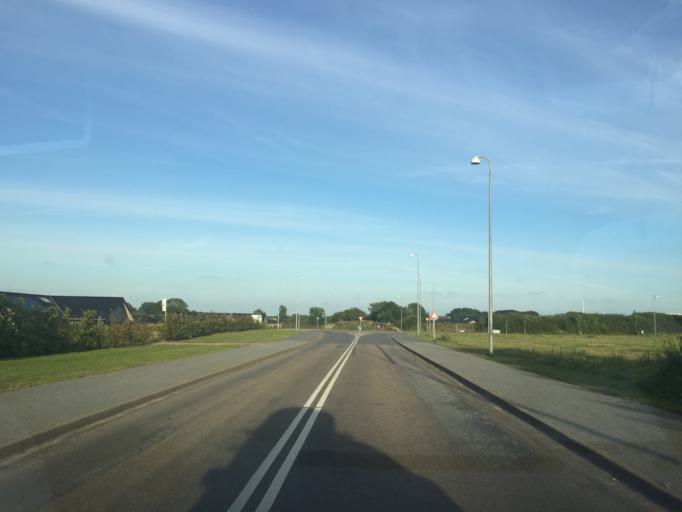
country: DK
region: South Denmark
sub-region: Kolding Kommune
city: Kolding
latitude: 55.4742
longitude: 9.5166
